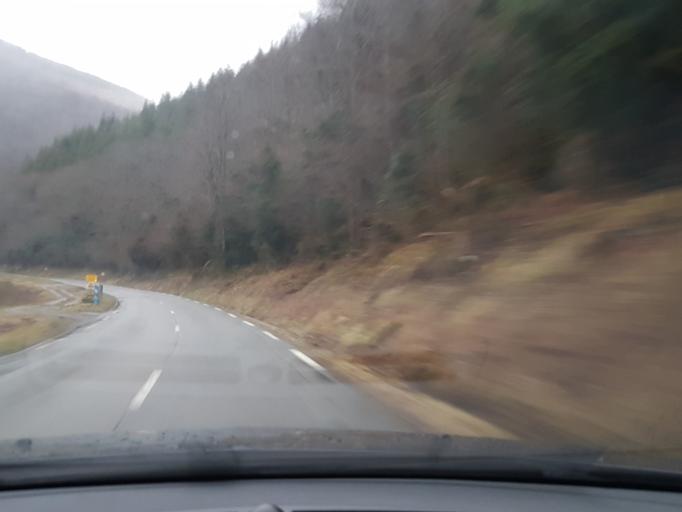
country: FR
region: Midi-Pyrenees
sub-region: Departement de l'Ariege
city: Saint-Girons
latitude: 42.9131
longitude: 1.1970
